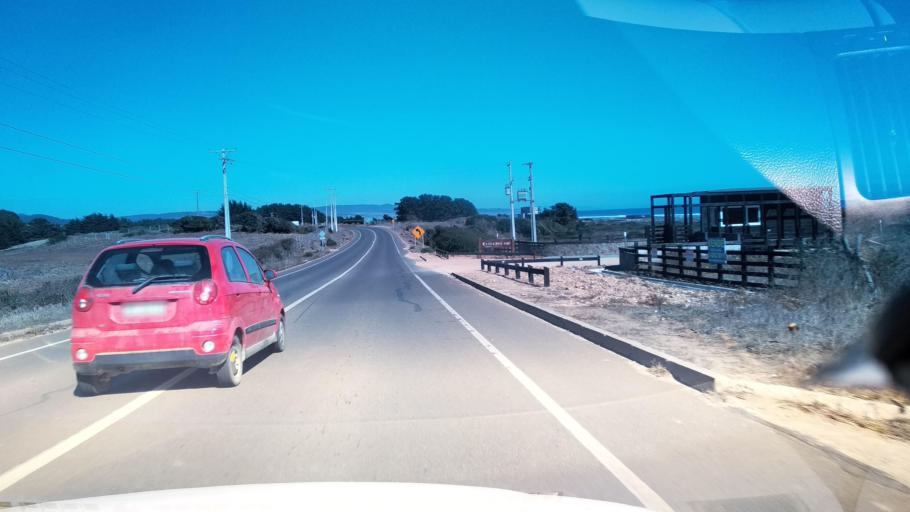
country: CL
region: O'Higgins
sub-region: Provincia de Colchagua
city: Santa Cruz
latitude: -34.4450
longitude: -72.0320
